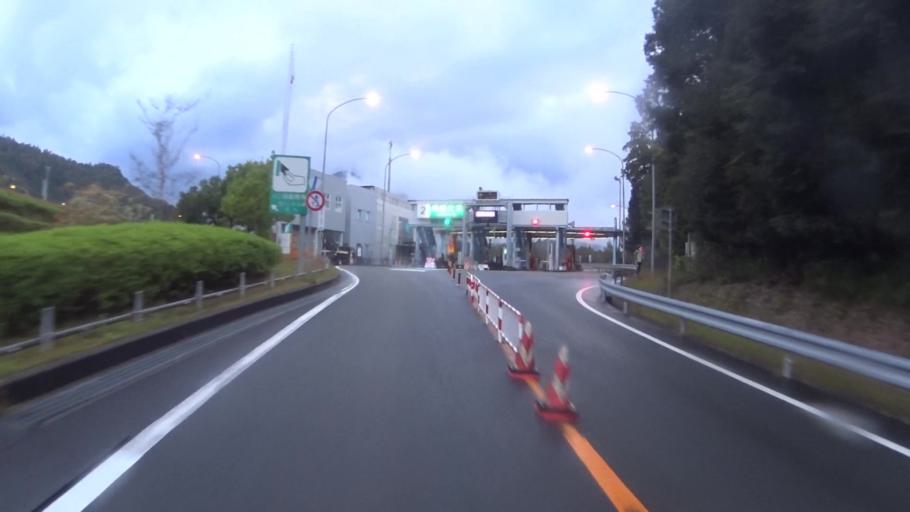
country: JP
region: Kyoto
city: Miyazu
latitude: 35.4317
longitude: 135.2080
